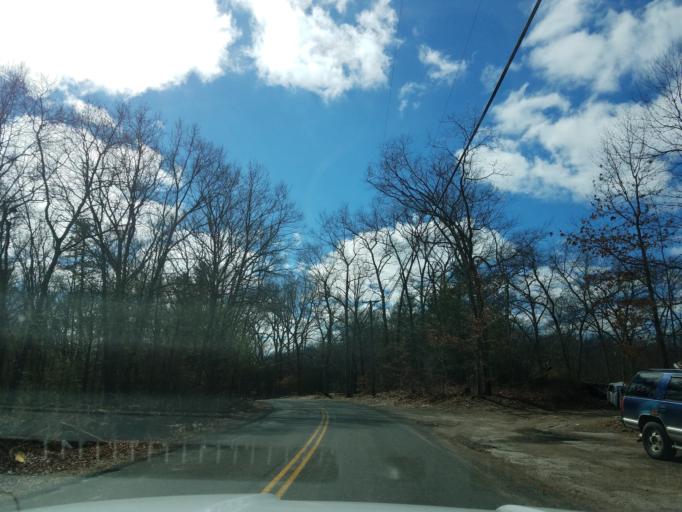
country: US
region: Connecticut
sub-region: Windham County
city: North Grosvenor Dale
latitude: 42.0124
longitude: -71.9162
